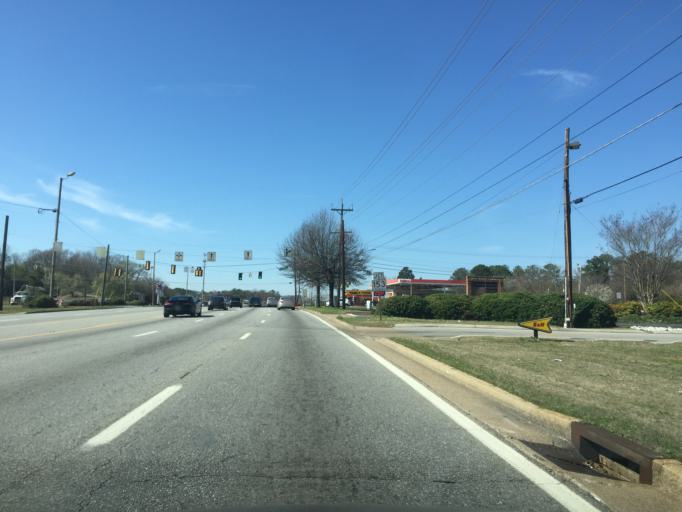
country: US
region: Tennessee
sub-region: Hamilton County
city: East Chattanooga
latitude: 35.0842
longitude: -85.2024
